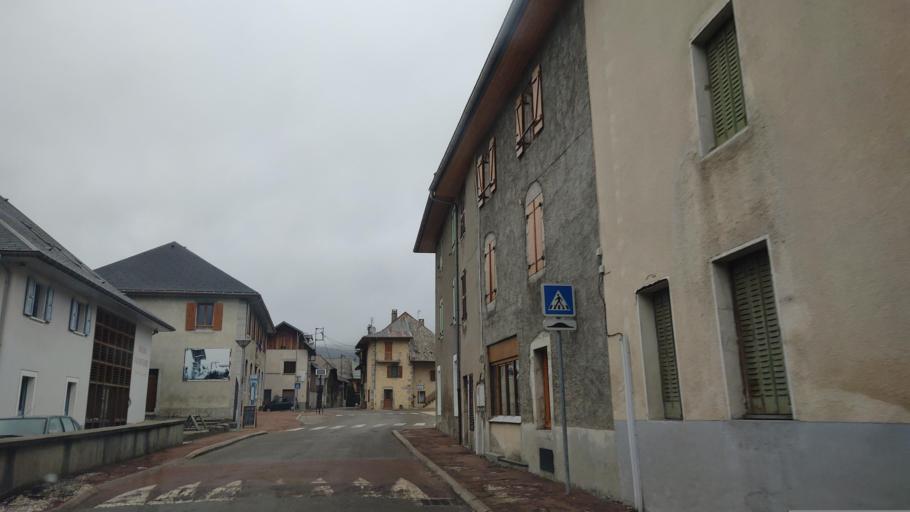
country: FR
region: Rhone-Alpes
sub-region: Departement de la Savoie
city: Gresy-sur-Isere
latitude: 45.6498
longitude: 6.1662
